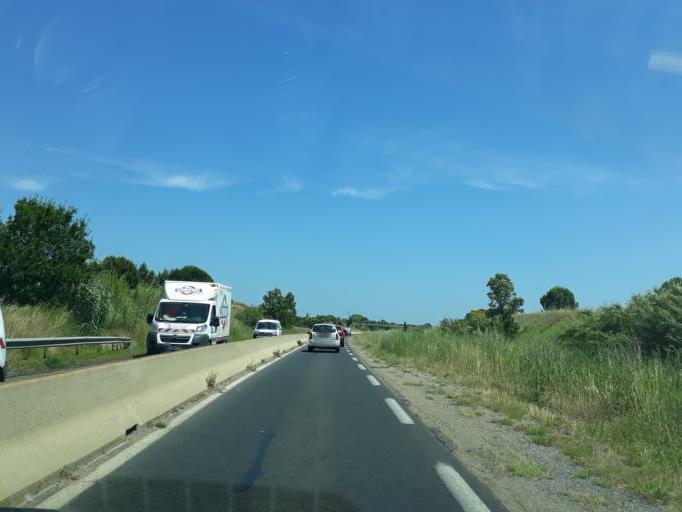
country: FR
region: Languedoc-Roussillon
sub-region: Departement de l'Herault
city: Vias
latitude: 43.3105
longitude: 3.4020
